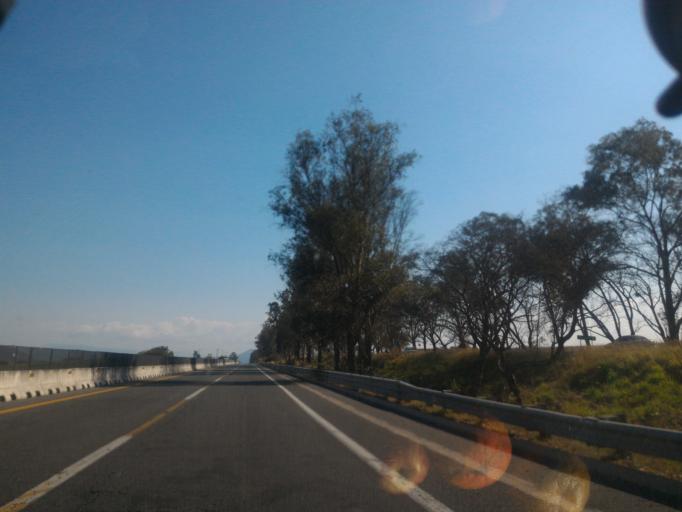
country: MX
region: Jalisco
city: Zapotiltic
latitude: 19.6144
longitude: -103.4600
